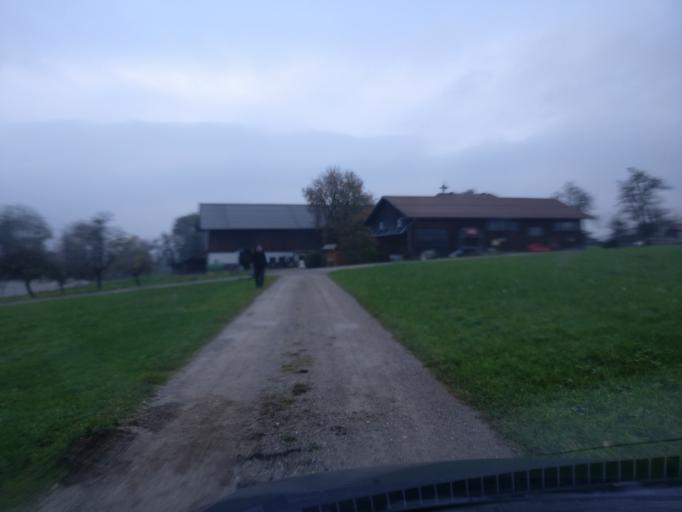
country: AT
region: Salzburg
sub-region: Politischer Bezirk Salzburg-Umgebung
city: Elixhausen
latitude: 47.8641
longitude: 13.0751
